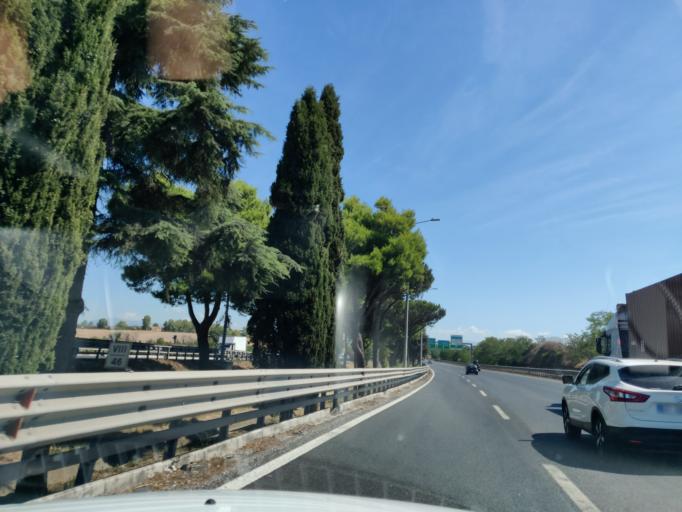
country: IT
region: Latium
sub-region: Citta metropolitana di Roma Capitale
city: Borgo Lotti
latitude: 41.8001
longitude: 12.5488
